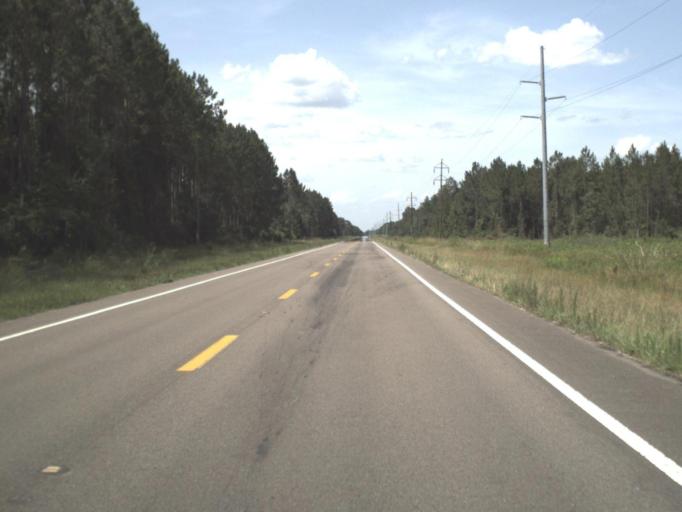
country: US
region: Florida
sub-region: Gilchrist County
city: Trenton
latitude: 29.6999
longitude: -82.7591
